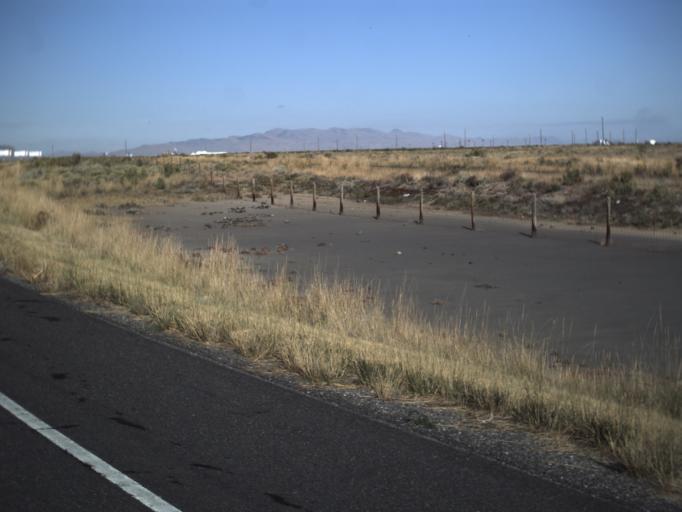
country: US
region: Utah
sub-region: Tooele County
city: Grantsville
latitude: 40.6861
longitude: -112.4475
